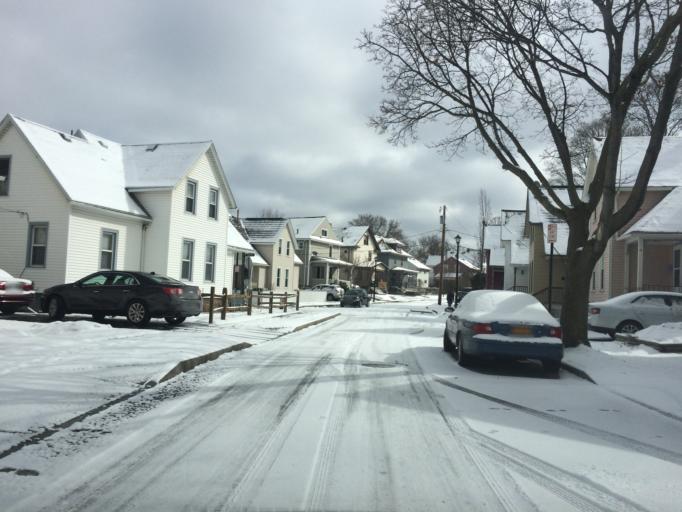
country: US
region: New York
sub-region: Monroe County
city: Rochester
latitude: 43.1390
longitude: -77.5936
